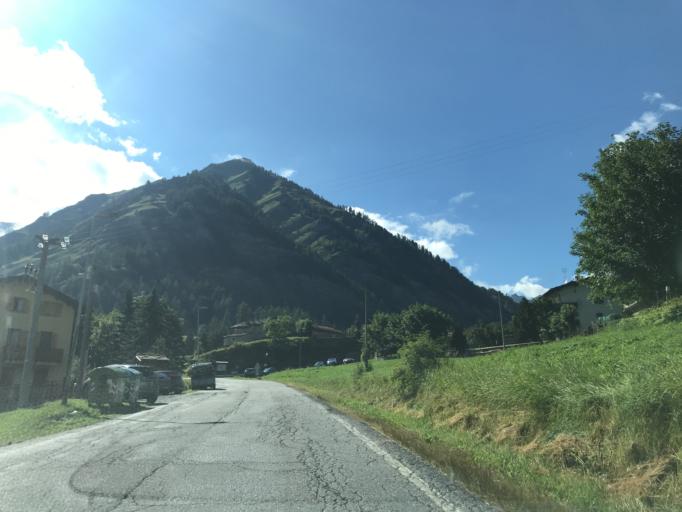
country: IT
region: Piedmont
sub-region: Provincia di Cuneo
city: Pontechianale
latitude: 44.6245
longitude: 7.0270
